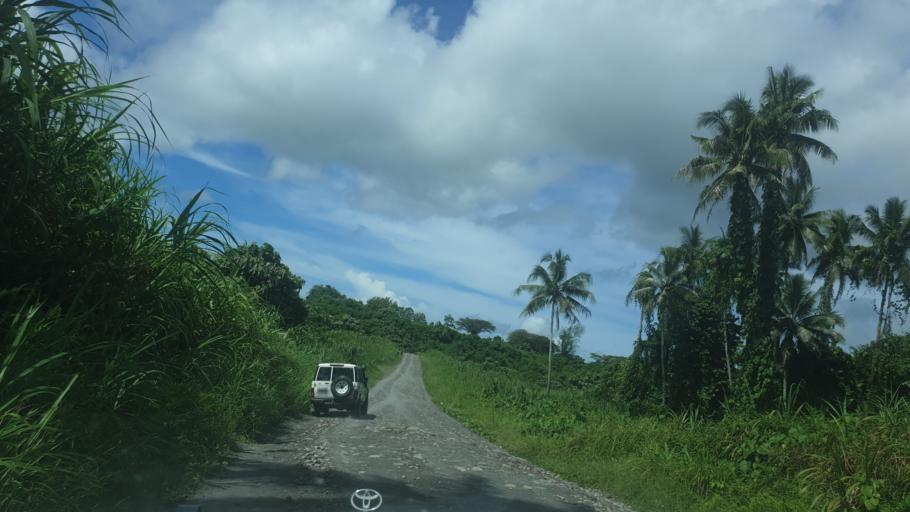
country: PG
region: Bougainville
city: Panguna
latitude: -6.5621
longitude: 155.3561
